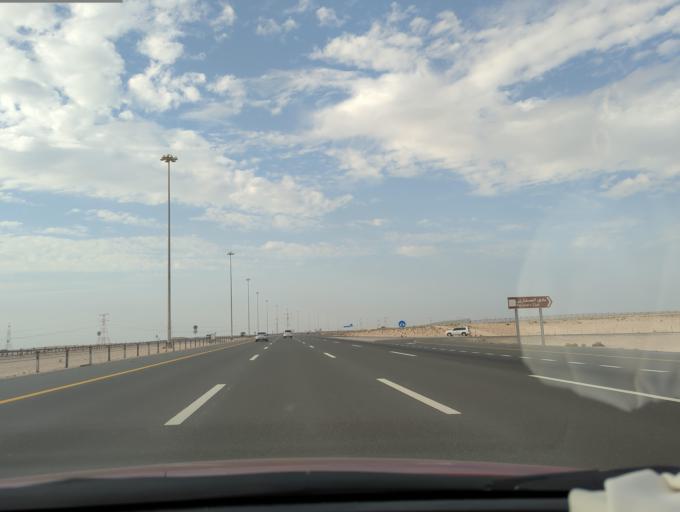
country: AE
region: Abu Dhabi
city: Abu Dhabi
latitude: 24.4434
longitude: 54.7572
